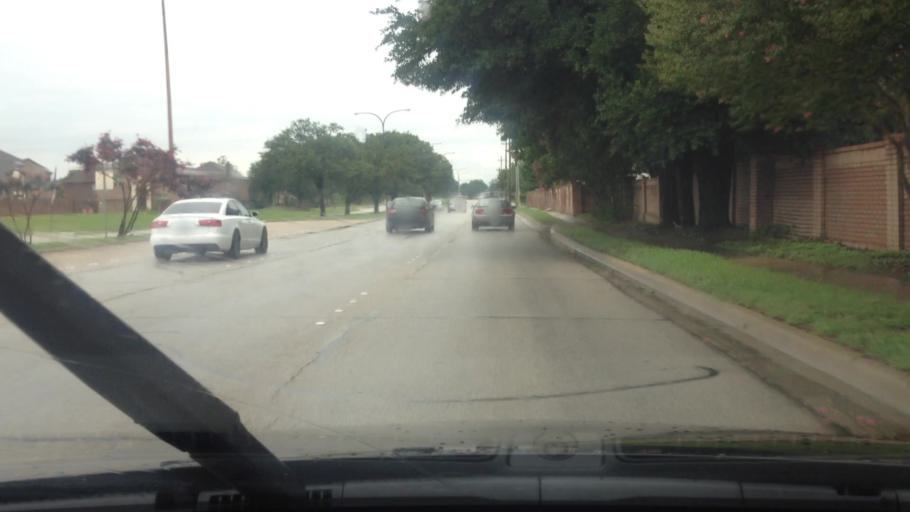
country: US
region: Texas
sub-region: Tarrant County
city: Watauga
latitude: 32.8508
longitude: -97.2899
